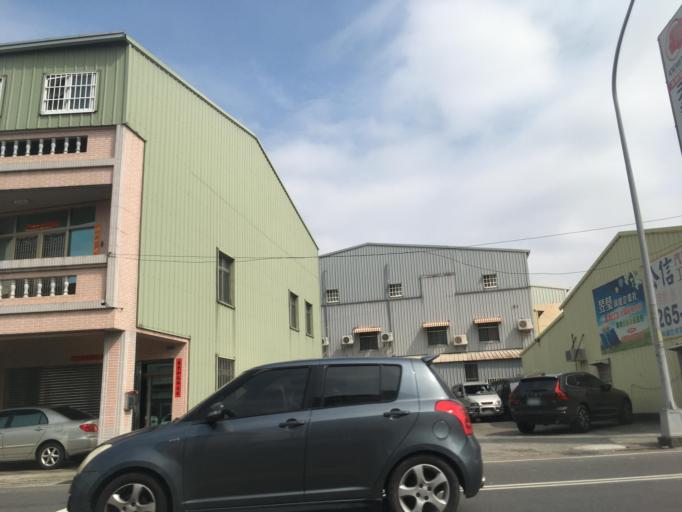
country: TW
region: Taiwan
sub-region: Yunlin
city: Douliu
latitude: 23.6913
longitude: 120.4677
